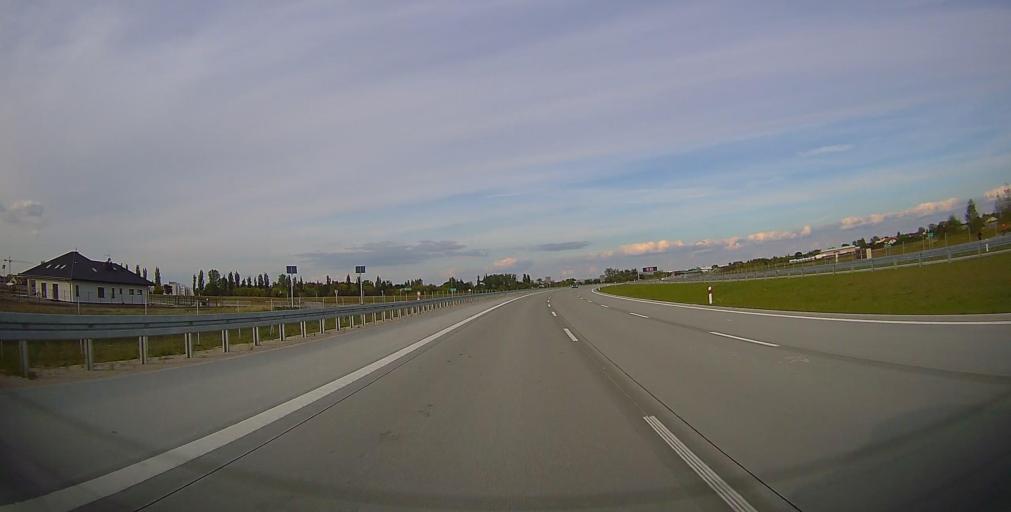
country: PL
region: Masovian Voivodeship
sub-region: Powiat piaseczynski
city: Lesznowola
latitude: 52.1050
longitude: 20.9711
